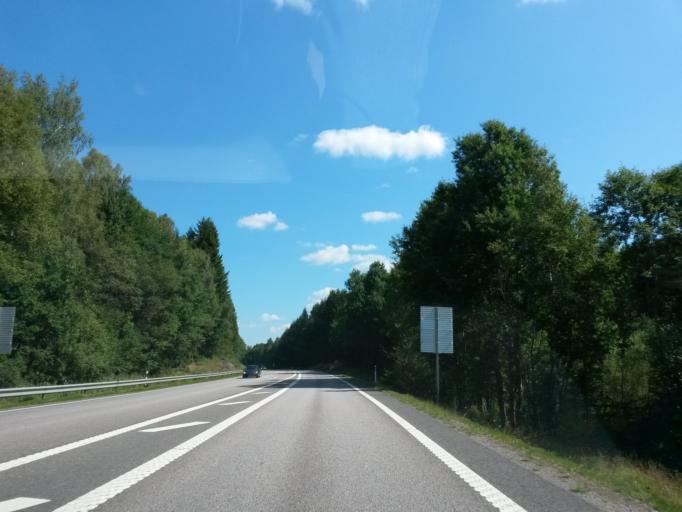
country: SE
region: Vaestra Goetaland
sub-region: Vargarda Kommun
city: Vargarda
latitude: 58.0464
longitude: 12.8086
